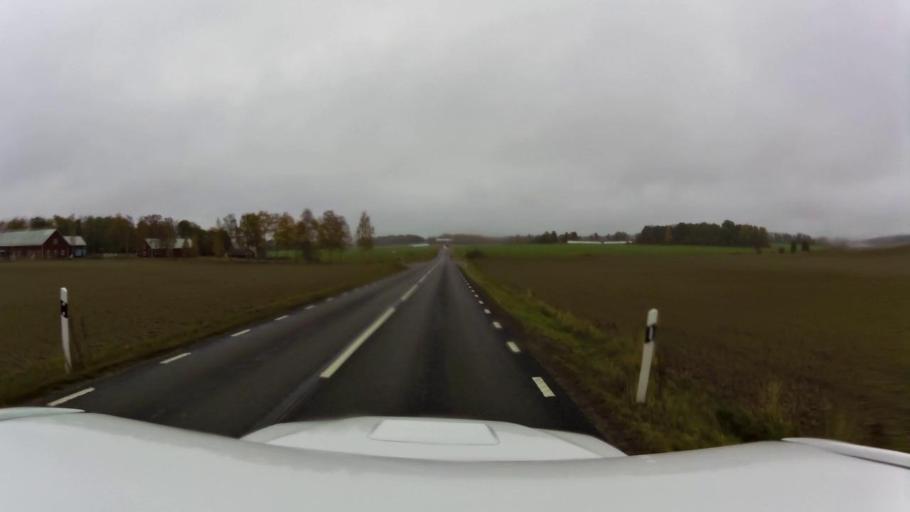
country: SE
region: OEstergoetland
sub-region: Linkopings Kommun
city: Linghem
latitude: 58.3941
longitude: 15.7723
